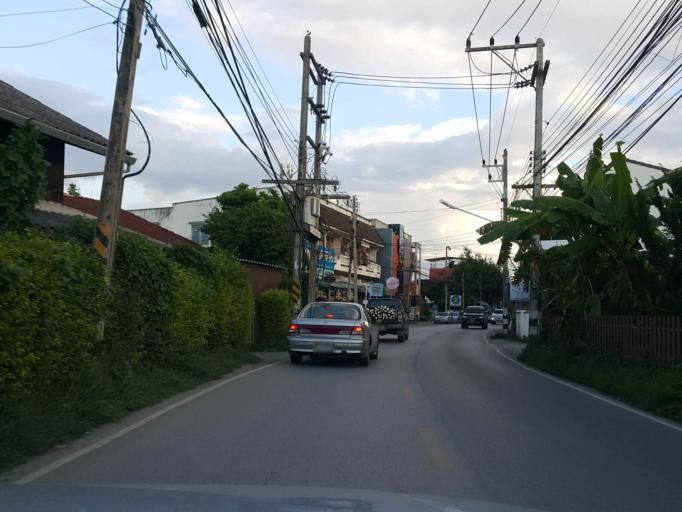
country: TH
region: Chiang Mai
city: Chiang Mai
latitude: 18.8065
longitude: 99.0053
